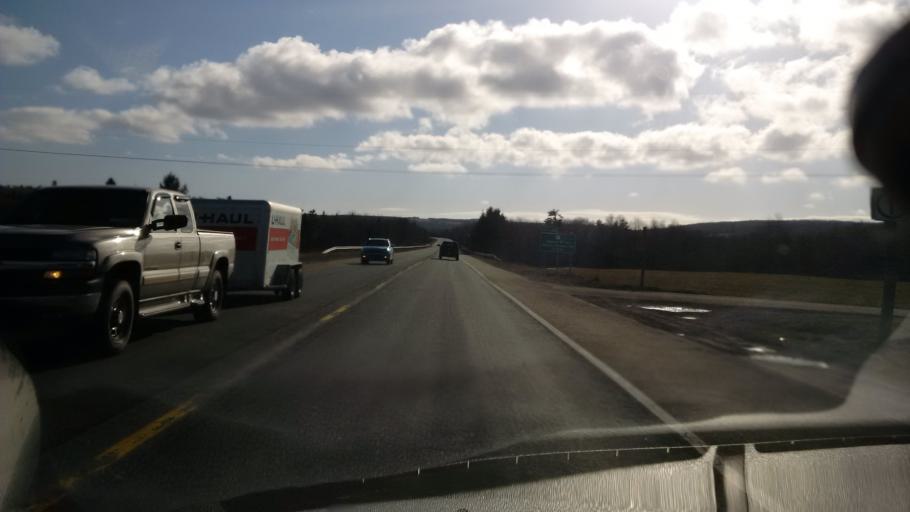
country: CA
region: Nova Scotia
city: Antigonish
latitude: 45.5789
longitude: -62.1017
